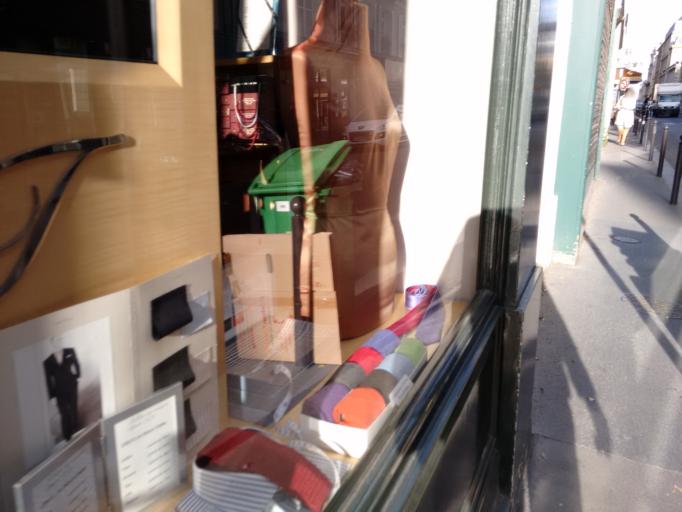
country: FR
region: Ile-de-France
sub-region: Paris
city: Paris
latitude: 48.8574
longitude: 2.3182
